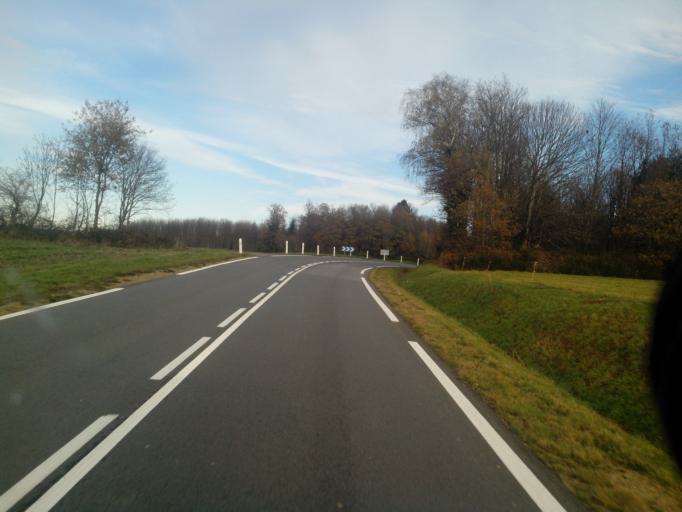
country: FR
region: Limousin
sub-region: Departement de la Haute-Vienne
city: Eymoutiers
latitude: 45.7384
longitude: 1.6957
